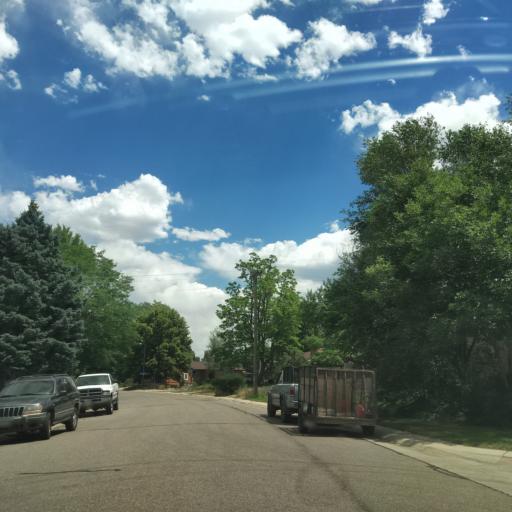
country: US
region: Colorado
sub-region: Jefferson County
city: Lakewood
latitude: 39.6881
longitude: -105.0853
